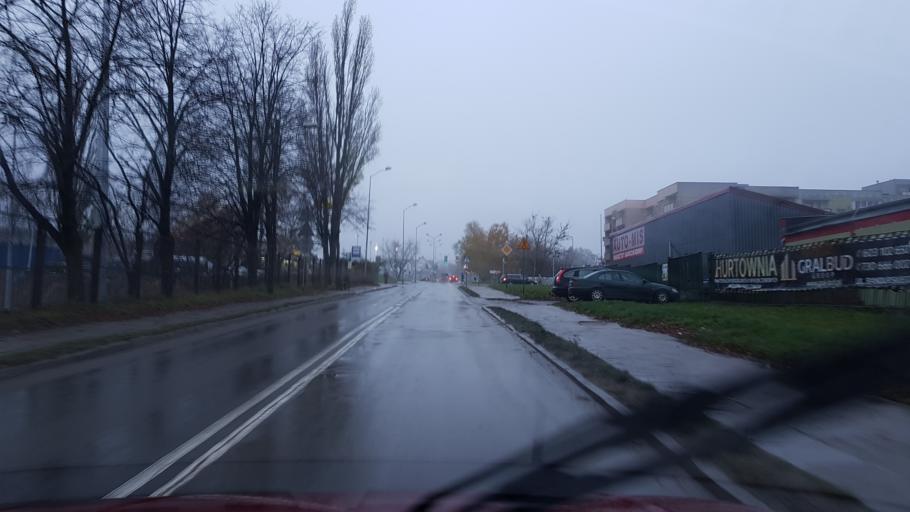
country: PL
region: West Pomeranian Voivodeship
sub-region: Szczecin
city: Szczecin
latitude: 53.4600
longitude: 14.5563
